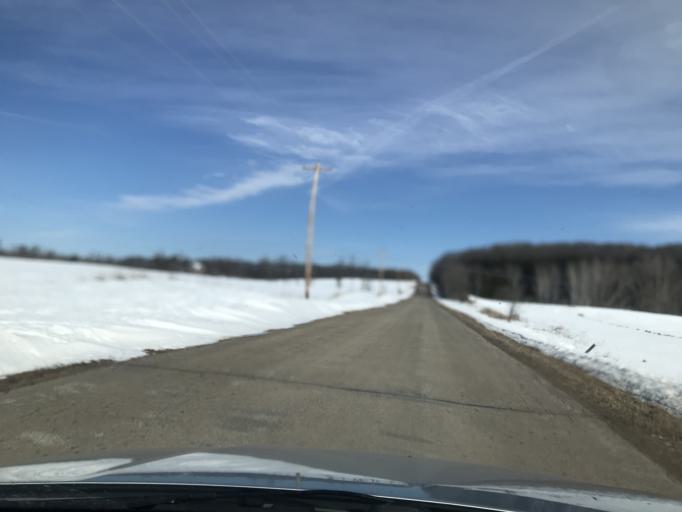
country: US
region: Wisconsin
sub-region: Oconto County
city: Gillett
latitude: 44.9634
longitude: -88.3061
